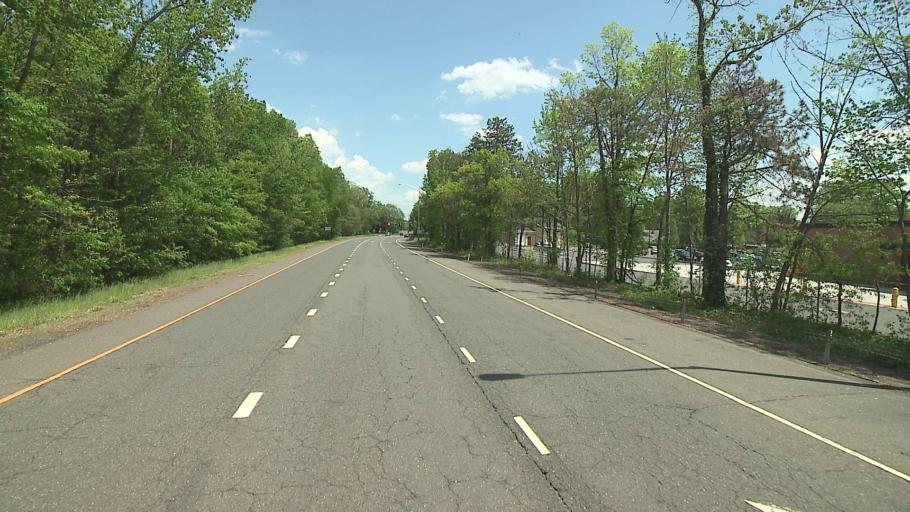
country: US
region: Connecticut
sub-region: Hartford County
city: New Britain
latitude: 41.6768
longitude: -72.8135
